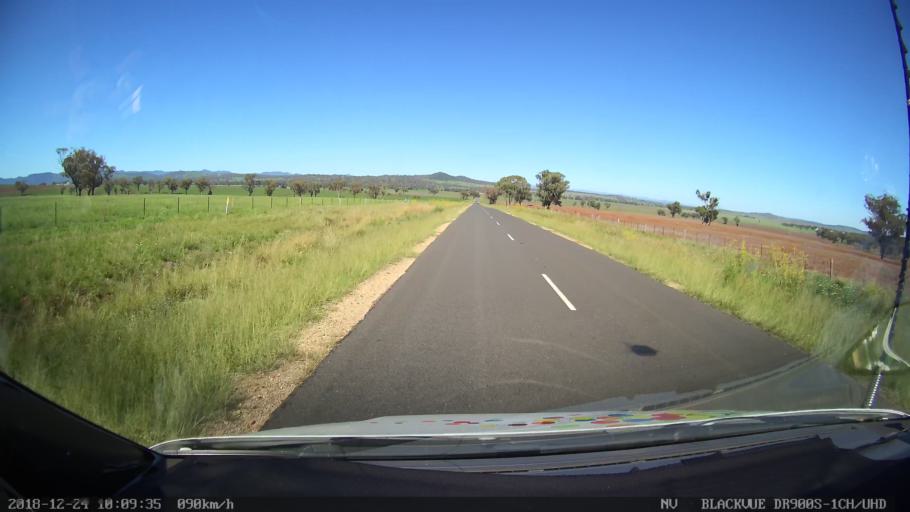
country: AU
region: New South Wales
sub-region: Liverpool Plains
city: Quirindi
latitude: -31.6642
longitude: 150.6886
